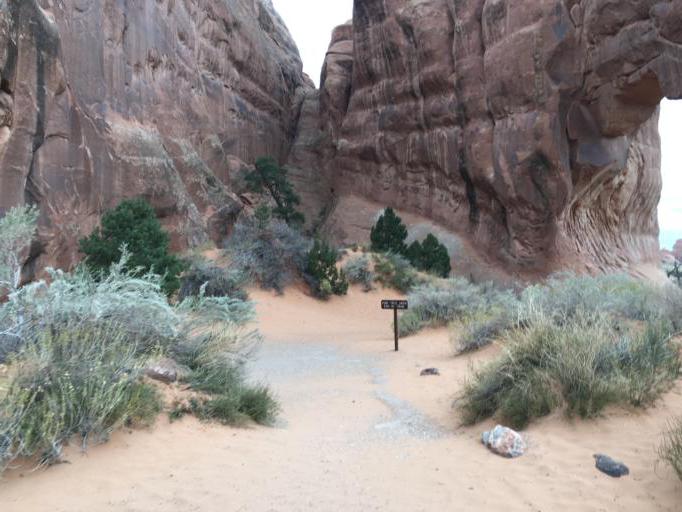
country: US
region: Utah
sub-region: Grand County
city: Moab
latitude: 38.7873
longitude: -109.5985
